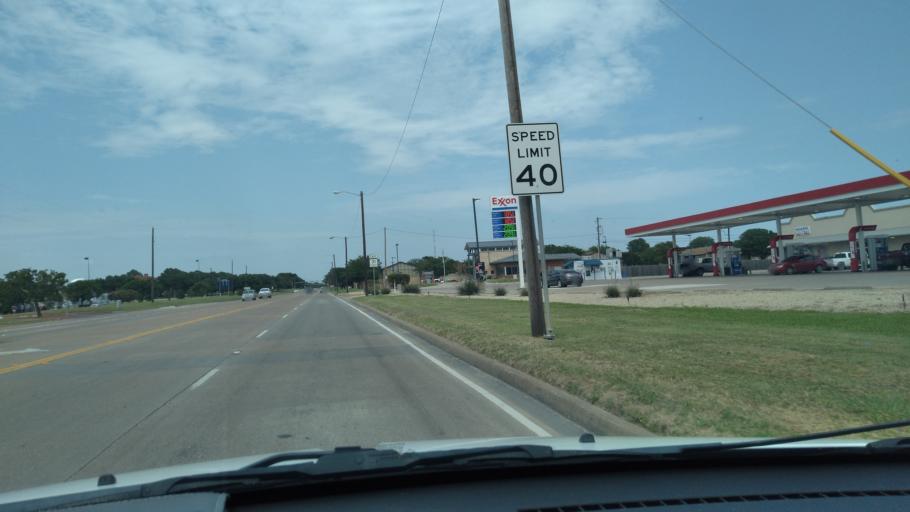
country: US
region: Texas
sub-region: Navarro County
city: Corsicana
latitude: 32.0711
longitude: -96.5033
